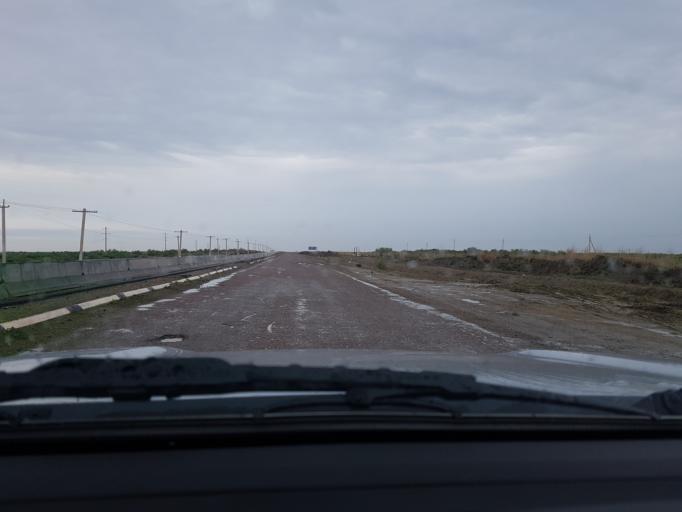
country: TM
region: Lebap
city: Farap
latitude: 39.2395
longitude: 63.7205
